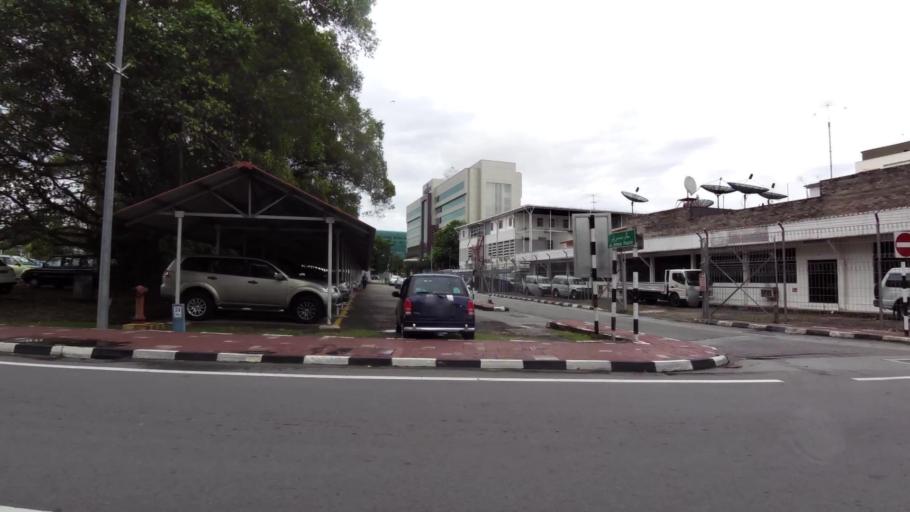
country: BN
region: Brunei and Muara
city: Bandar Seri Begawan
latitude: 4.8915
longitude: 114.9404
